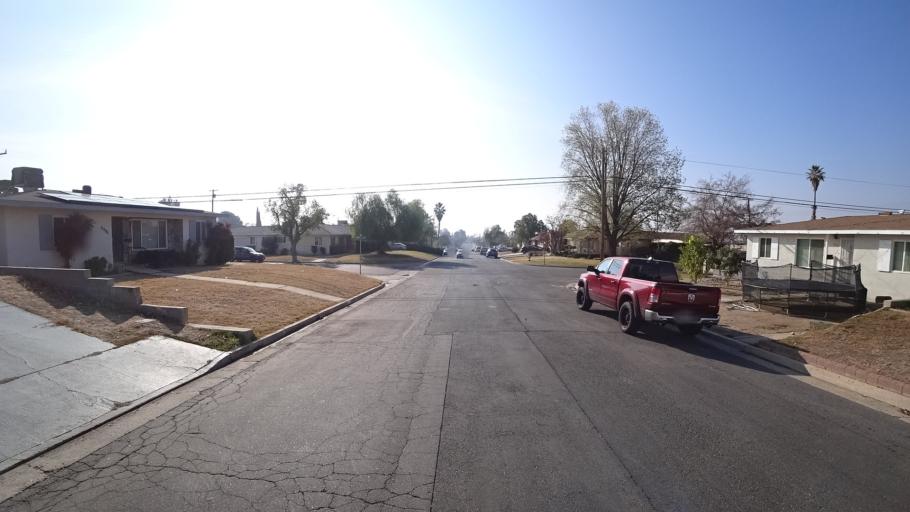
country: US
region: California
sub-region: Kern County
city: Oildale
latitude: 35.3996
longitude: -118.9786
